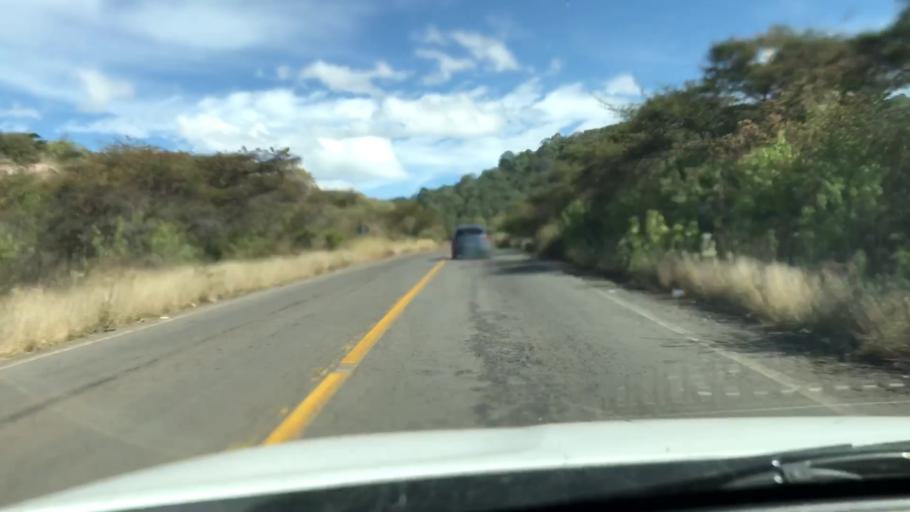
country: MX
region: Jalisco
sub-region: Zacoalco de Torres
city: Barranca de Otates (Barranca de Otatan)
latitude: 20.1925
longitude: -103.6992
